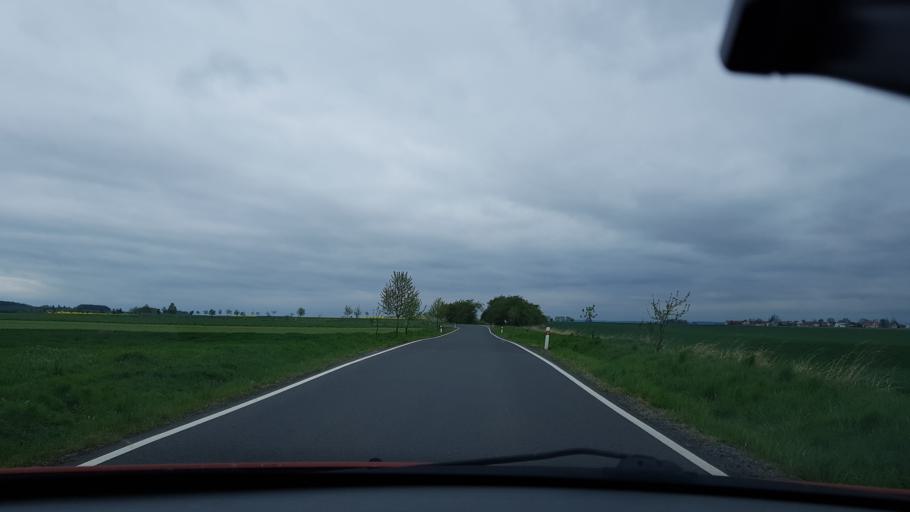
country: CZ
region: Olomoucky
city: Vidnava
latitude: 50.3760
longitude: 17.1747
